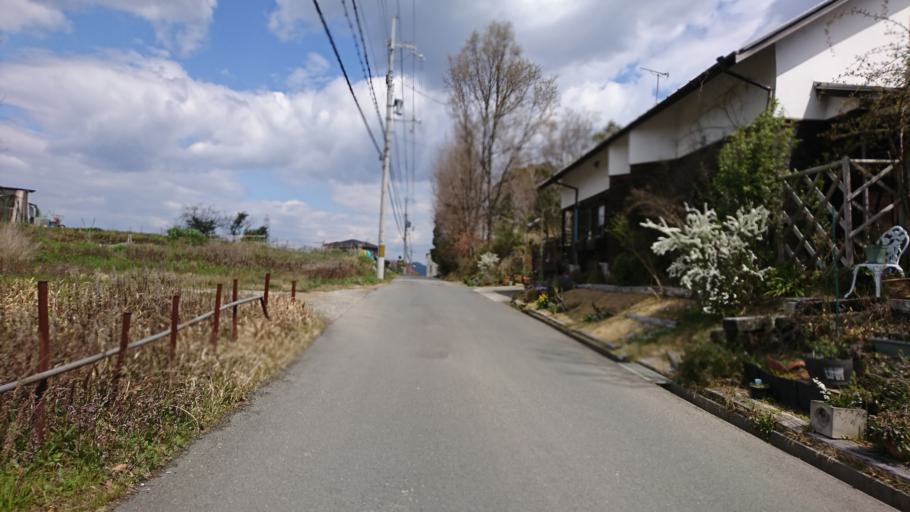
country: JP
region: Hyogo
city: Kakogawacho-honmachi
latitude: 34.7743
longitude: 134.8722
